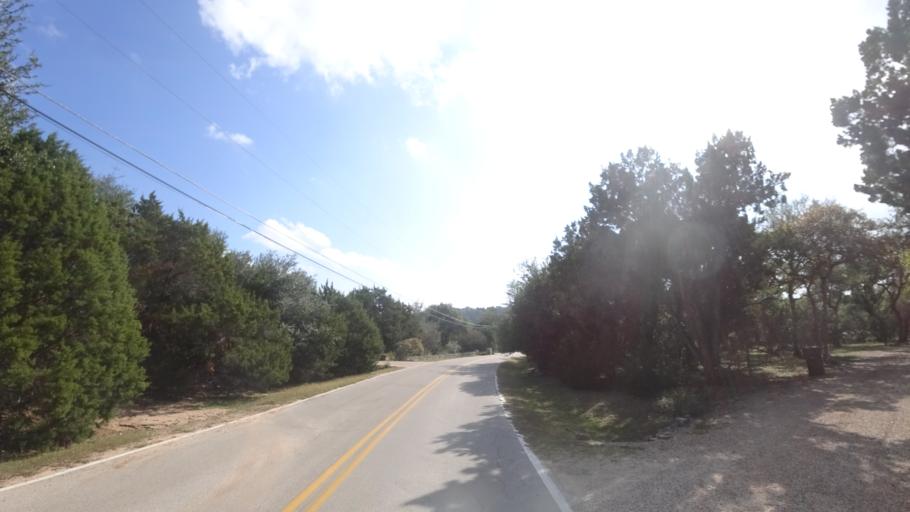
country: US
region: Texas
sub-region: Travis County
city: Barton Creek
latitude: 30.3020
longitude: -97.8624
